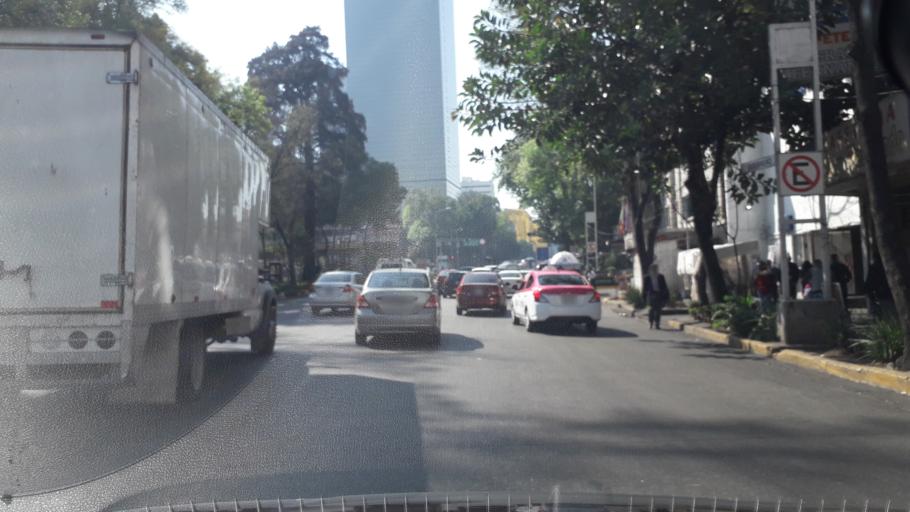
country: MX
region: Mexico City
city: Cuauhtemoc
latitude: 19.4392
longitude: -99.1489
